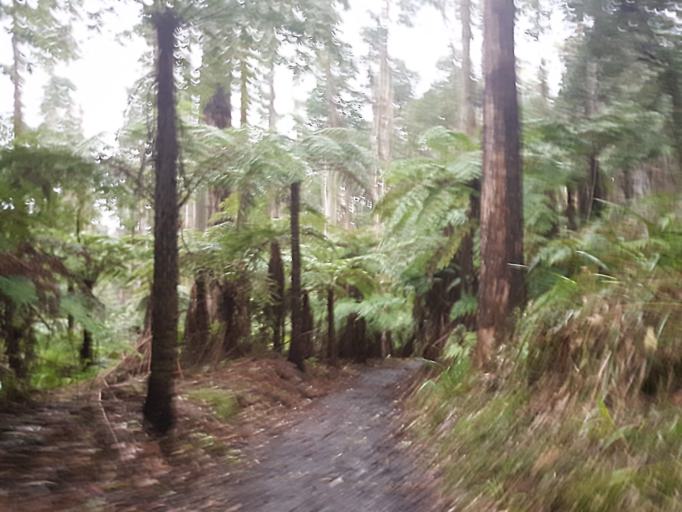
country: AU
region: Victoria
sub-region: Yarra Ranges
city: Belgrave
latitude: -37.8965
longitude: 145.3520
